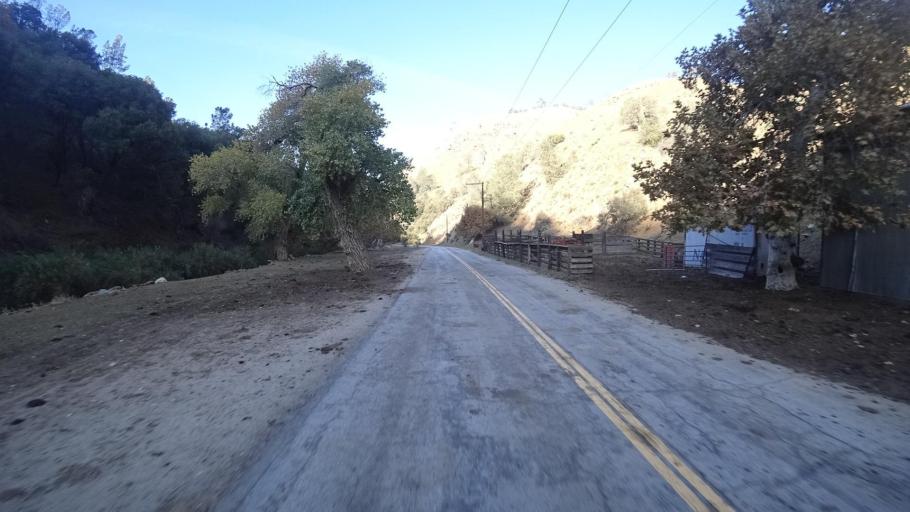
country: US
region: California
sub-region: Kern County
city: Golden Hills
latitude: 35.3150
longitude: -118.5140
